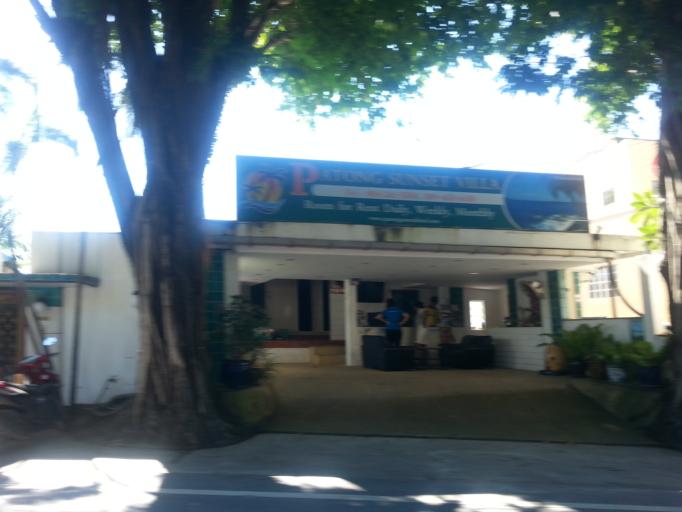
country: TH
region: Phuket
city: Patong
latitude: 7.9099
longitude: 98.2962
